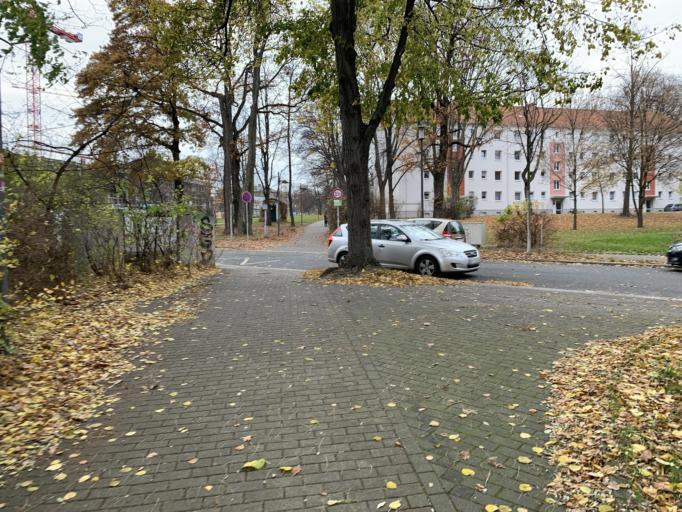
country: DE
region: Saxony
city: Dresden
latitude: 51.0335
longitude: 13.7301
